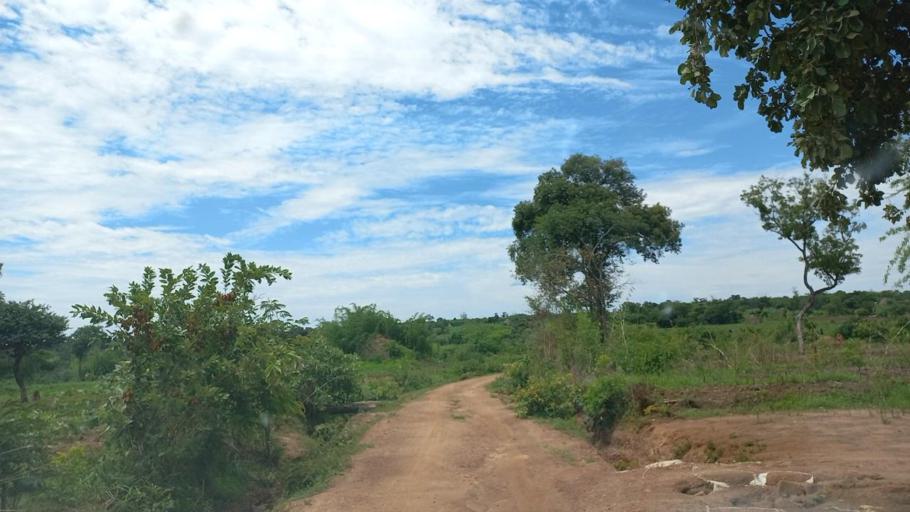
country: ZM
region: Copperbelt
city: Kitwe
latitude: -12.8164
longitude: 28.3898
